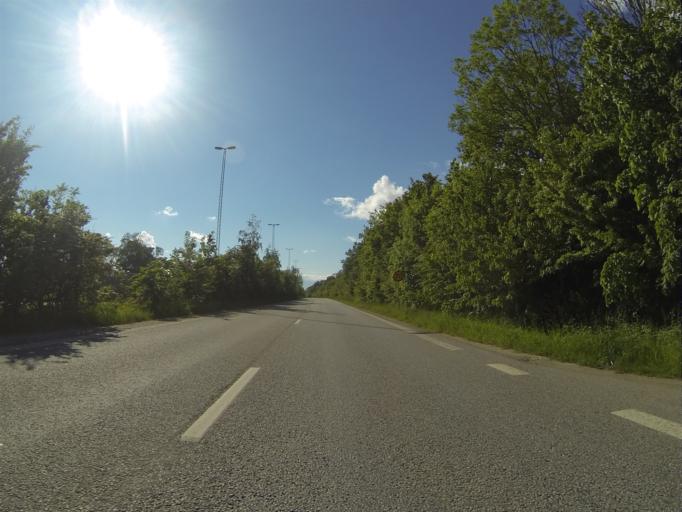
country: SE
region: Skane
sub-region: Lunds Kommun
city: Lund
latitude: 55.6930
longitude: 13.2391
